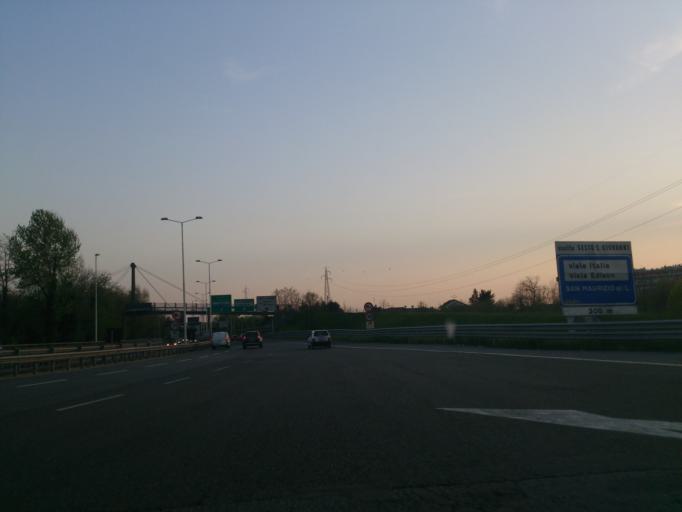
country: IT
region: Lombardy
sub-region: Citta metropolitana di Milano
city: Cologno Monzese
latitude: 45.5508
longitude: 9.2621
